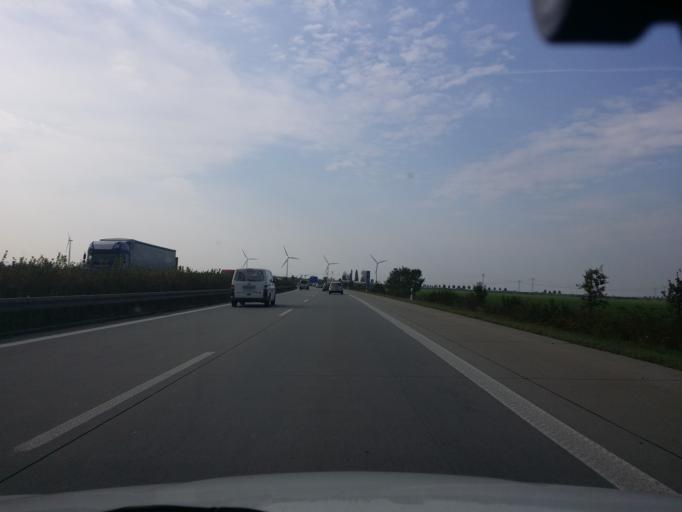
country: DE
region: Saxony
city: Zwenkau
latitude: 51.2625
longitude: 12.2794
